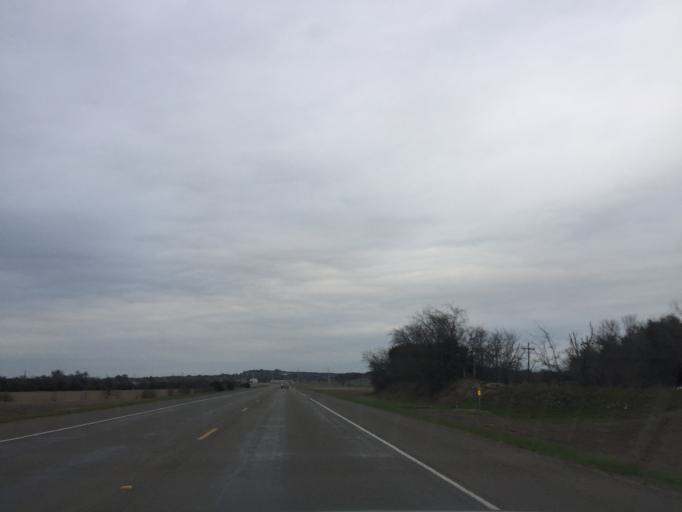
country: US
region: Texas
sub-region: Coryell County
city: Gatesville
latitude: 31.4618
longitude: -97.7168
